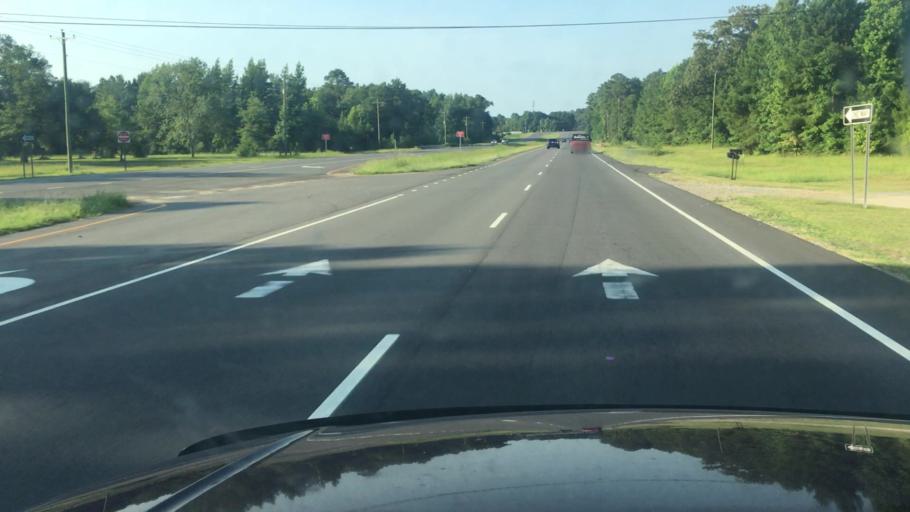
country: US
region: North Carolina
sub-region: Cumberland County
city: Hope Mills
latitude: 34.9437
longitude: -78.8474
